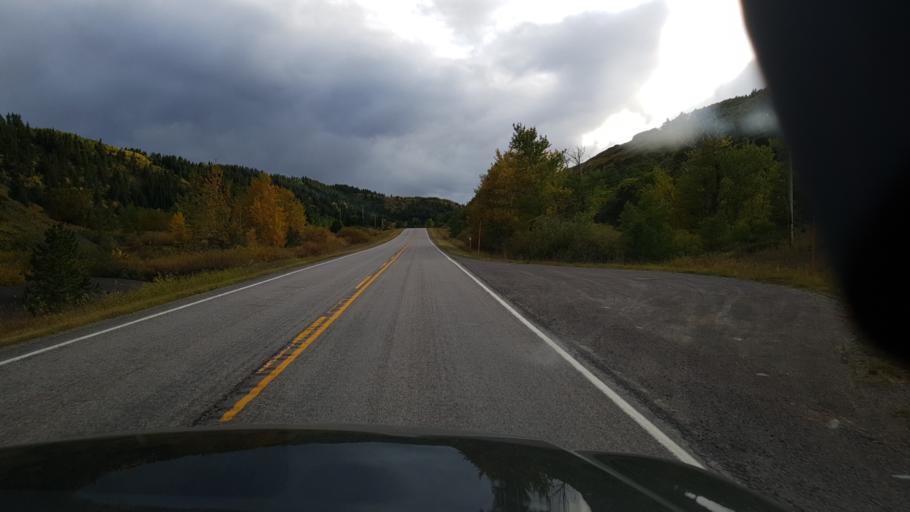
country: US
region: Montana
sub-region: Glacier County
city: South Browning
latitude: 48.3531
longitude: -113.3023
